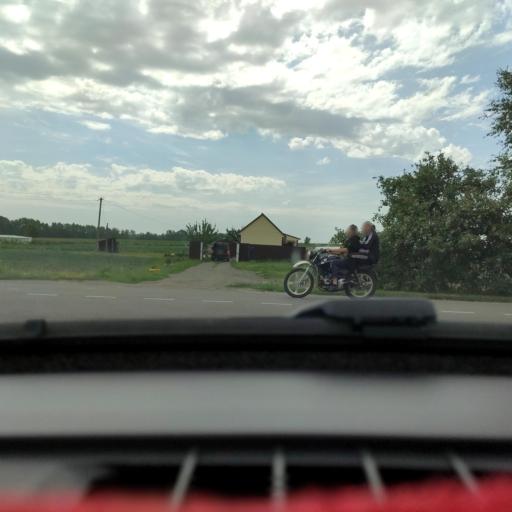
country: RU
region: Voronezj
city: Davydovka
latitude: 51.1925
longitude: 39.4950
